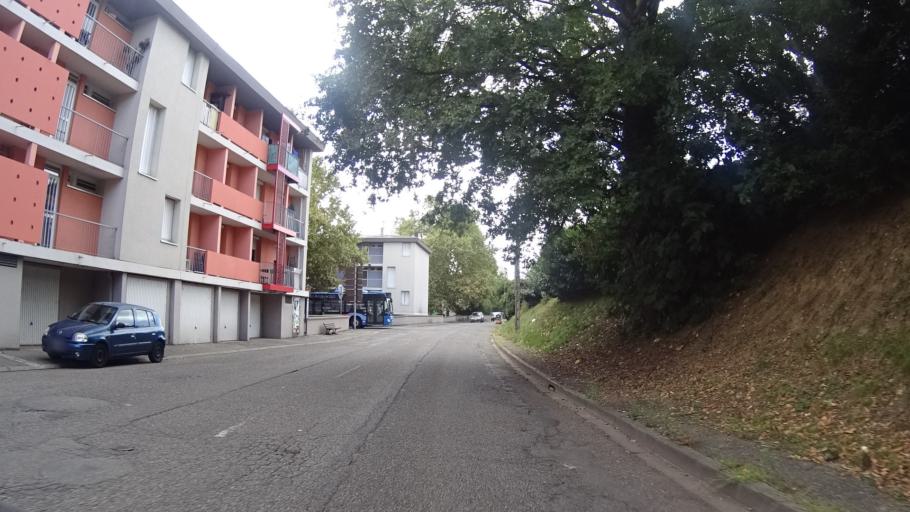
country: FR
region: Aquitaine
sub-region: Departement du Lot-et-Garonne
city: Agen
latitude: 44.2134
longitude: 0.6455
